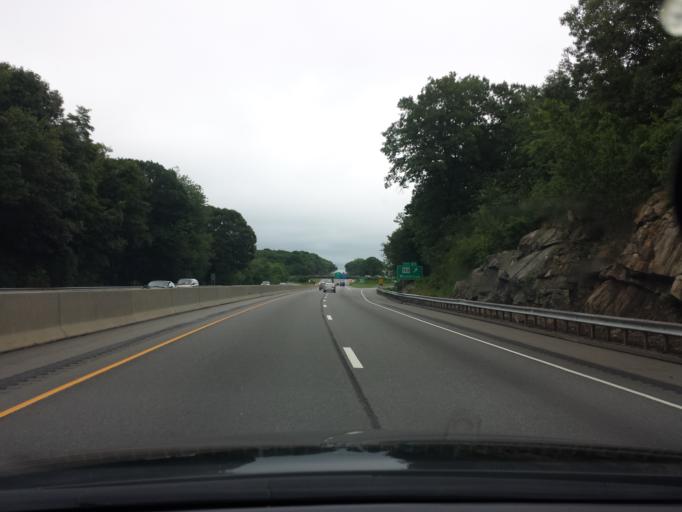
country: US
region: Connecticut
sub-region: Middlesex County
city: Westbrook Center
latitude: 41.2920
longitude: -72.4498
